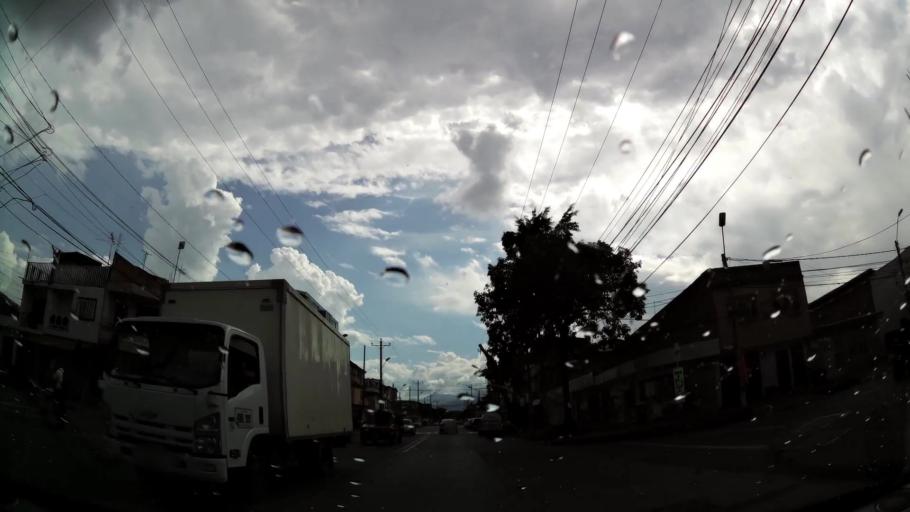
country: CO
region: Valle del Cauca
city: Cali
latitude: 3.4753
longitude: -76.5091
